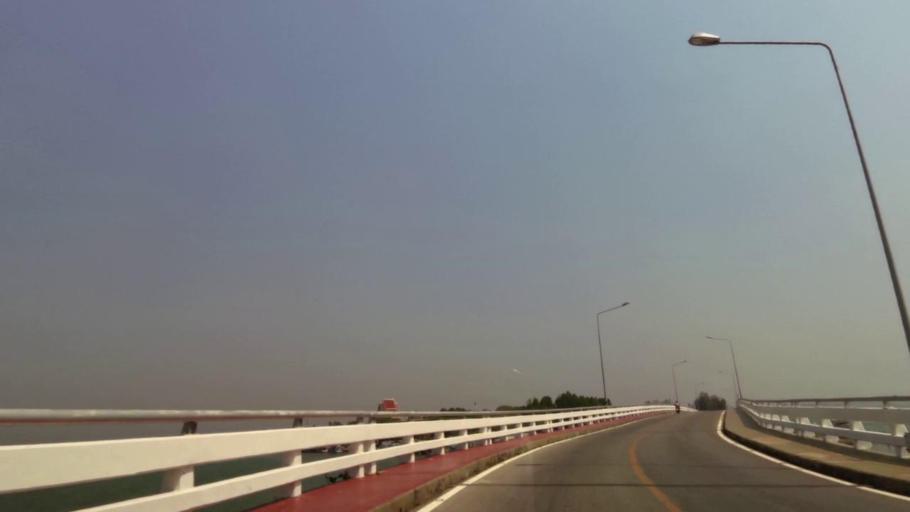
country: TH
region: Chanthaburi
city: Tha Mai
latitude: 12.5389
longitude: 101.9482
